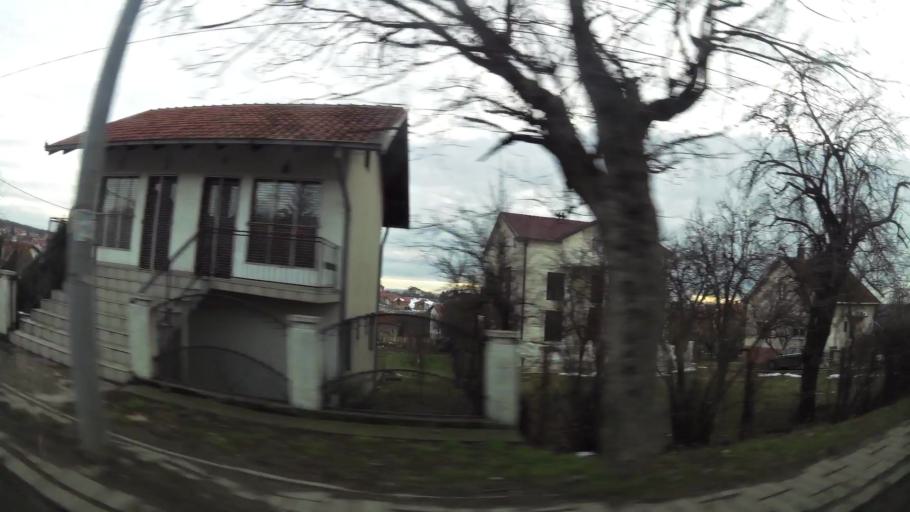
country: RS
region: Central Serbia
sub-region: Belgrade
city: Vozdovac
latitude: 44.7429
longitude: 20.4821
